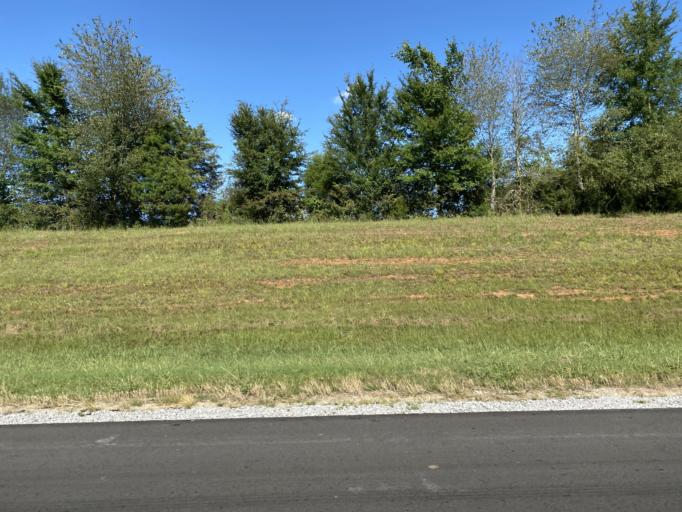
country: US
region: Alabama
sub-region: Limestone County
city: Athens
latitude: 34.7527
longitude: -86.9380
